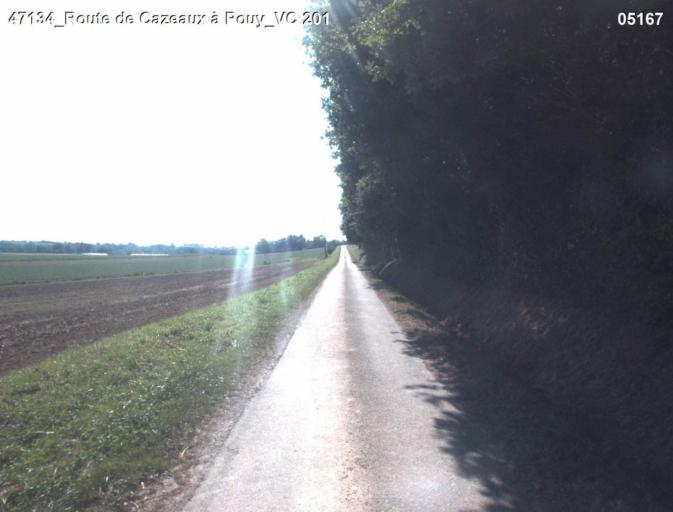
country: FR
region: Aquitaine
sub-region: Departement du Lot-et-Garonne
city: Mezin
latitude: 44.0416
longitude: 0.3106
